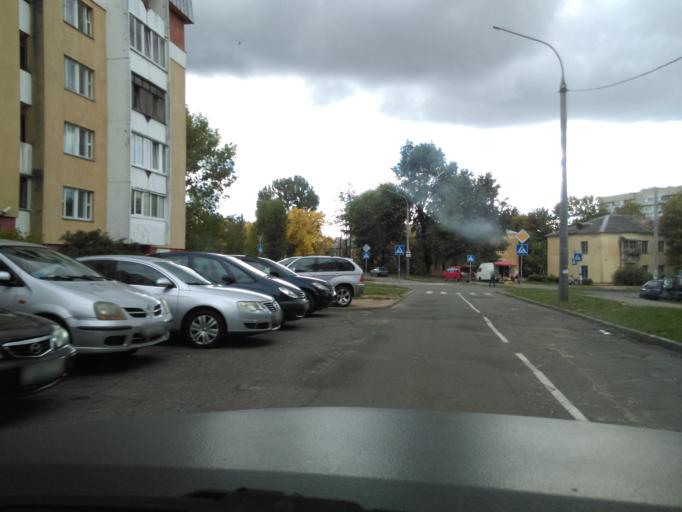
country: BY
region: Minsk
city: Minsk
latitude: 53.9096
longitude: 27.6288
